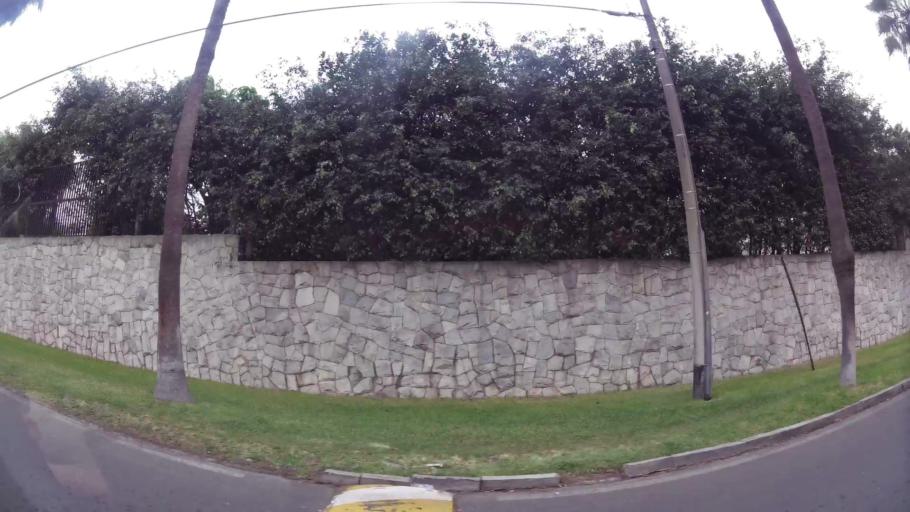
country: PE
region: Lima
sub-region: Lima
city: La Molina
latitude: -12.0806
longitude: -76.9166
